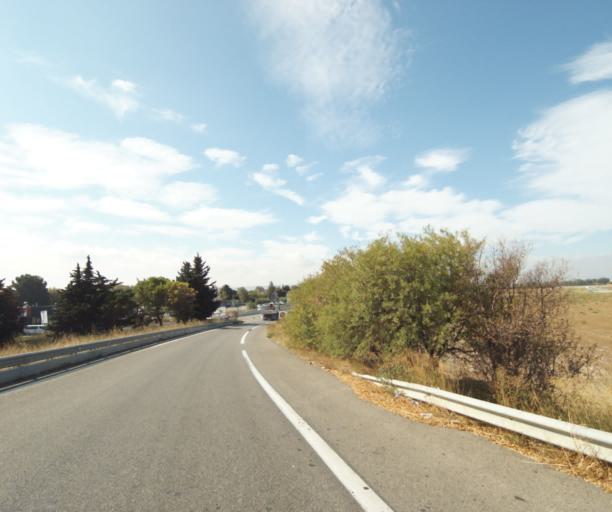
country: FR
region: Provence-Alpes-Cote d'Azur
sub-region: Departement des Bouches-du-Rhone
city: Saint-Victoret
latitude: 43.4247
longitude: 5.2346
